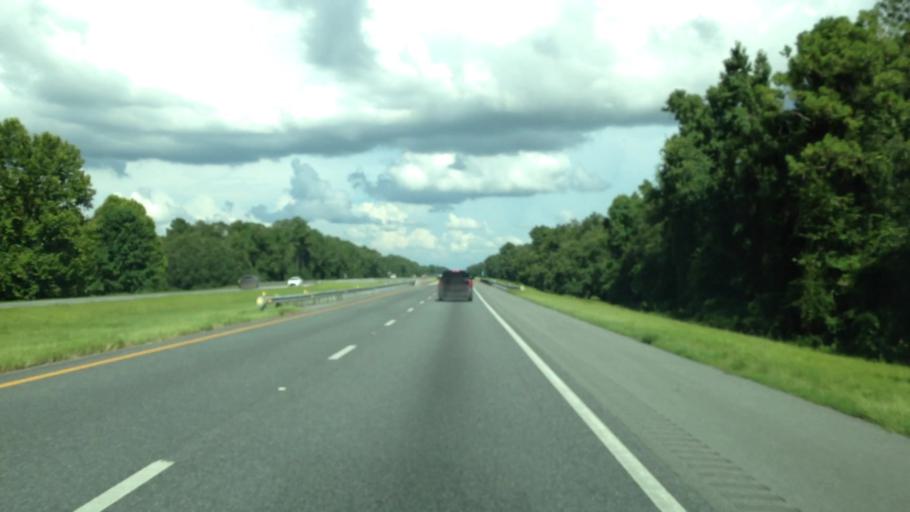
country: US
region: Florida
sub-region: Madison County
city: Madison
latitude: 30.3615
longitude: -83.2166
